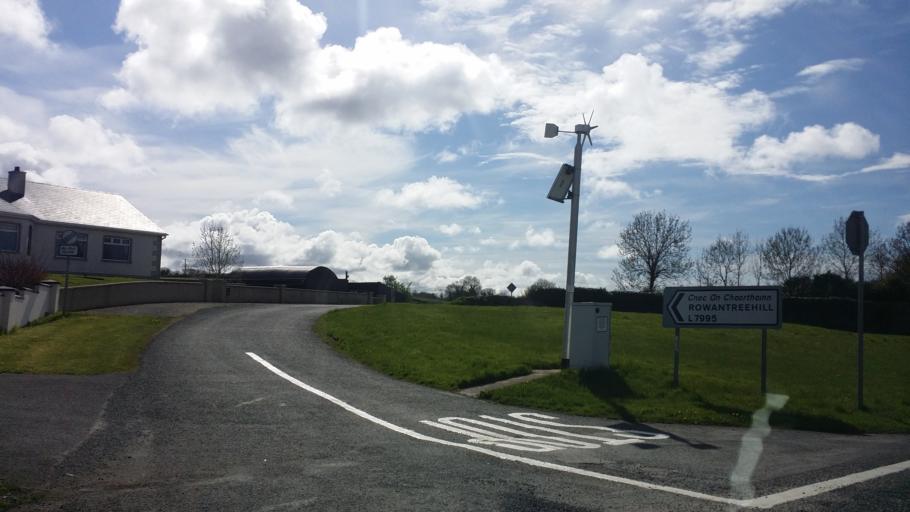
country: IE
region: Ulster
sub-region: County Donegal
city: Ballyshannon
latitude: 54.4844
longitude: -8.1248
